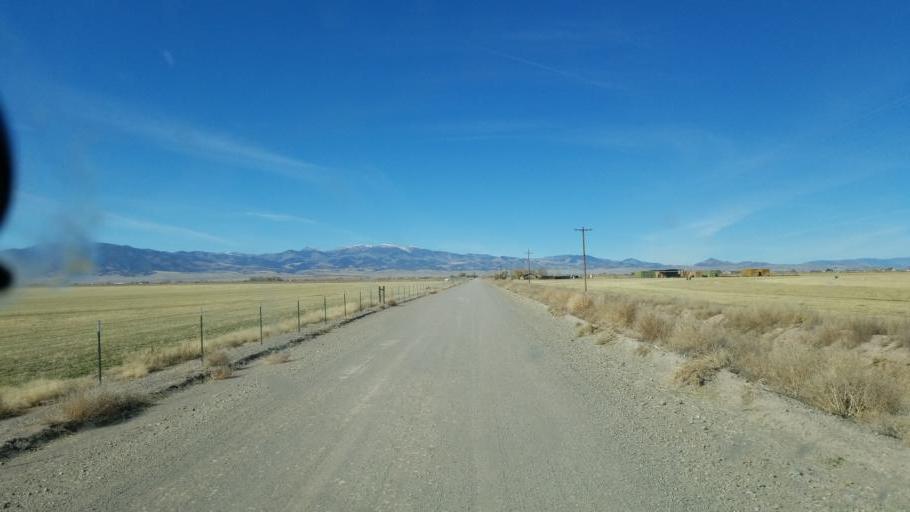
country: US
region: Colorado
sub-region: Rio Grande County
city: Monte Vista
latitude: 37.5313
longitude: -106.0611
